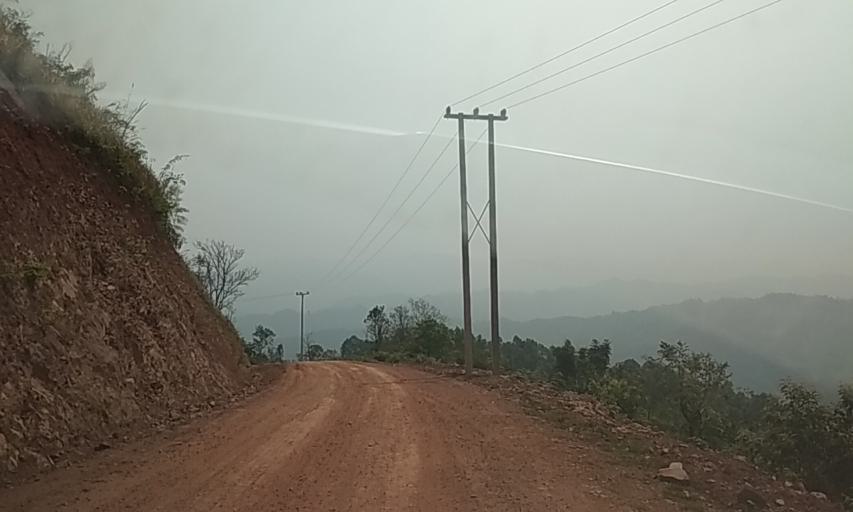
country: VN
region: Huyen Dien Bien
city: Dien Bien Phu
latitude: 21.4990
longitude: 102.7904
